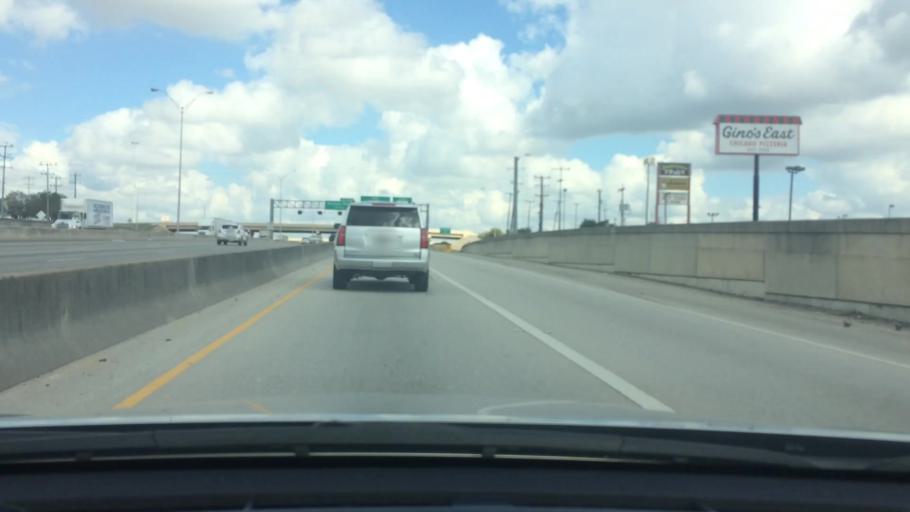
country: US
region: Texas
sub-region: Bexar County
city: Live Oak
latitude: 29.5649
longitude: -98.3365
